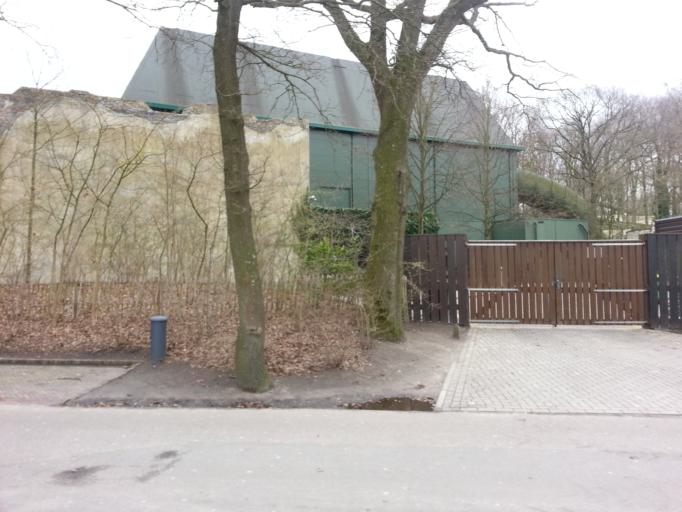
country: NL
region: North Brabant
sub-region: Gemeente Loon op Zand
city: Loon op Zand
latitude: 51.6484
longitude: 5.0461
